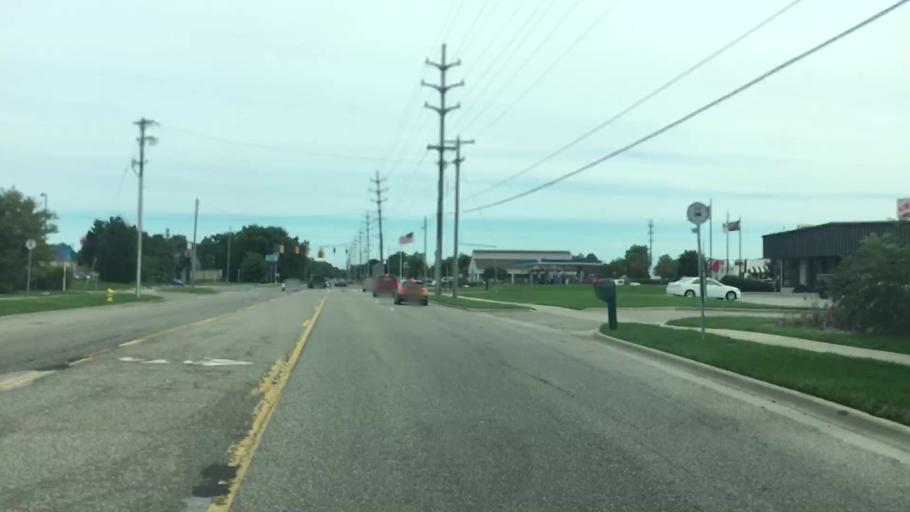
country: US
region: Michigan
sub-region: Ottawa County
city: Jenison
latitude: 42.8839
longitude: -85.7822
